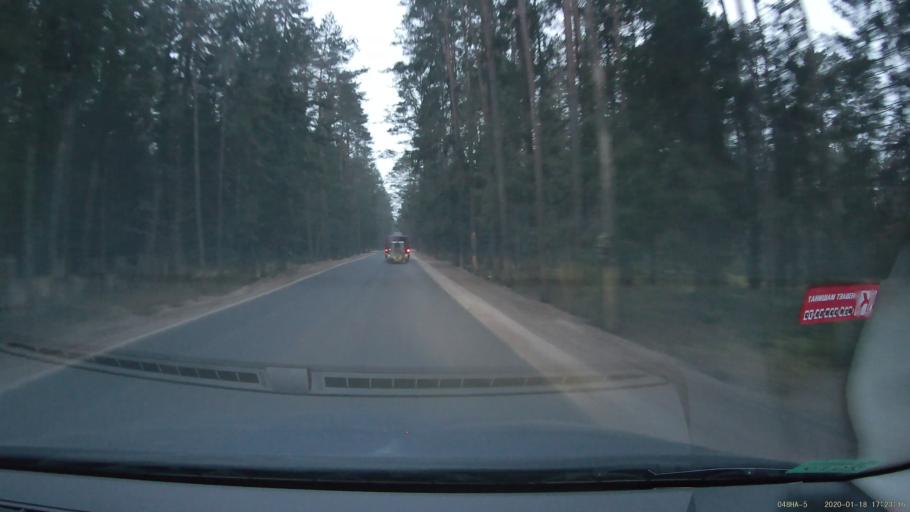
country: BY
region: Minsk
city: Rakaw
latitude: 53.9584
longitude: 27.1183
